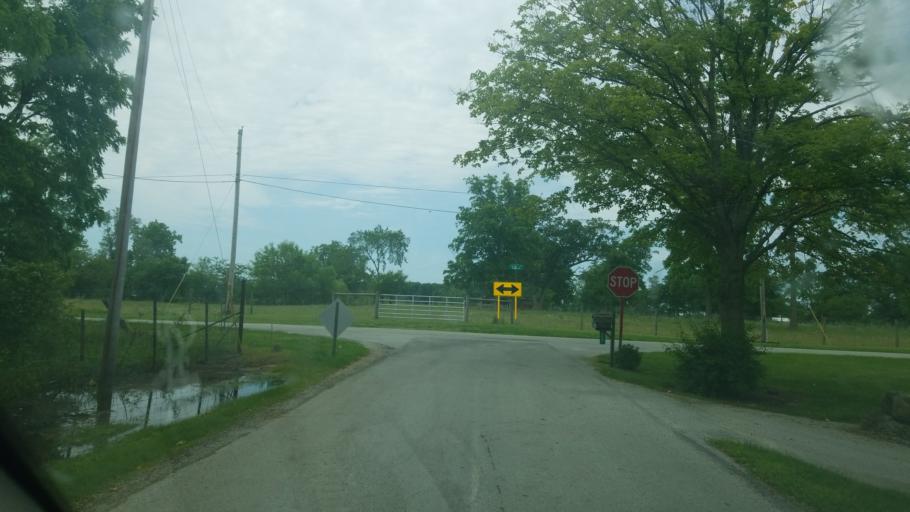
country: US
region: Ohio
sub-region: Wood County
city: North Baltimore
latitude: 41.2329
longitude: -83.6208
